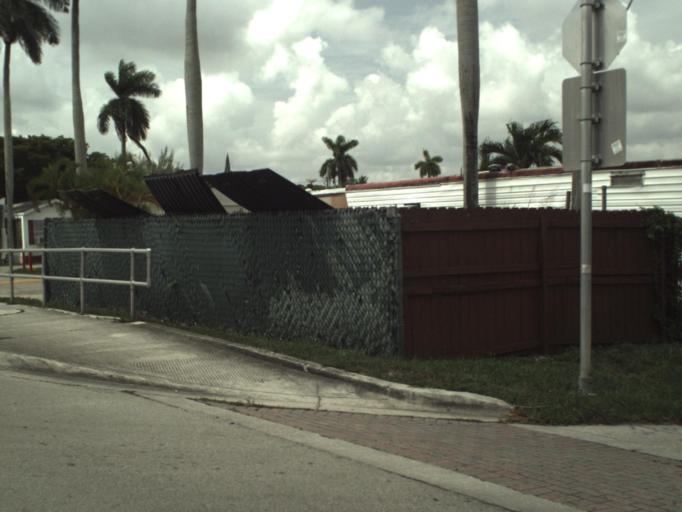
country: US
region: Florida
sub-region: Broward County
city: Hallandale Beach
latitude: 25.9783
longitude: -80.1422
